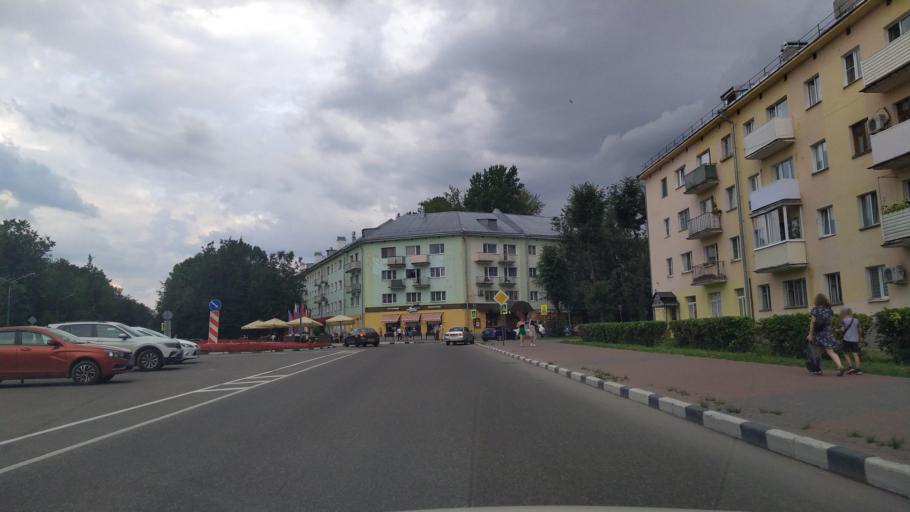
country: RU
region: Novgorod
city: Velikiy Novgorod
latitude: 58.5205
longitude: 31.2689
